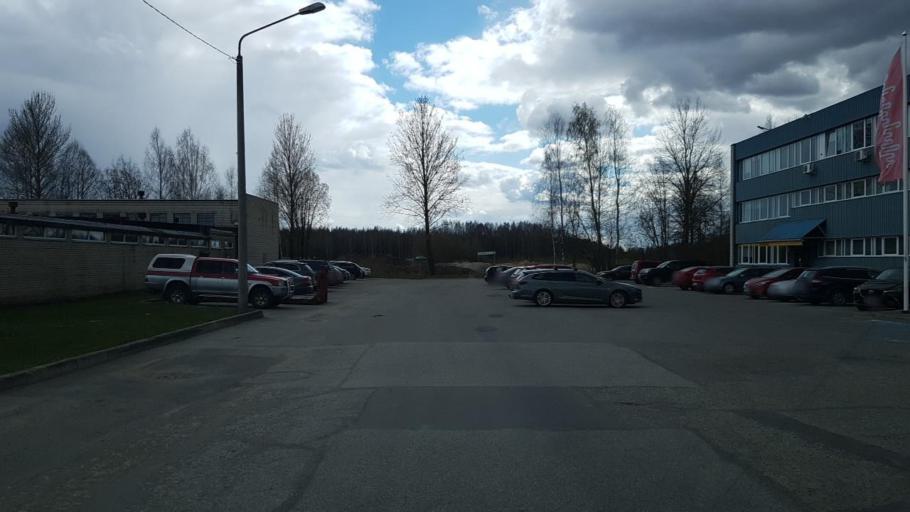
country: EE
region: Tartu
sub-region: UElenurme vald
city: Ulenurme
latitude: 58.3400
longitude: 26.7313
